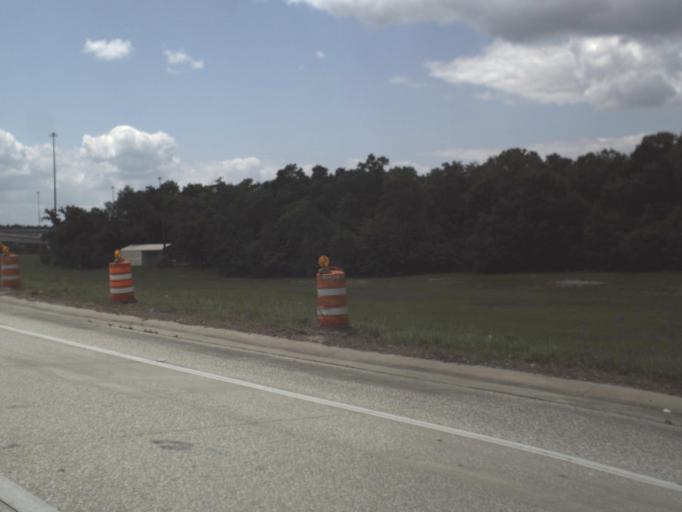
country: US
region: Florida
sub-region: Saint Johns County
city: Fruit Cove
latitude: 30.1664
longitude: -81.5507
